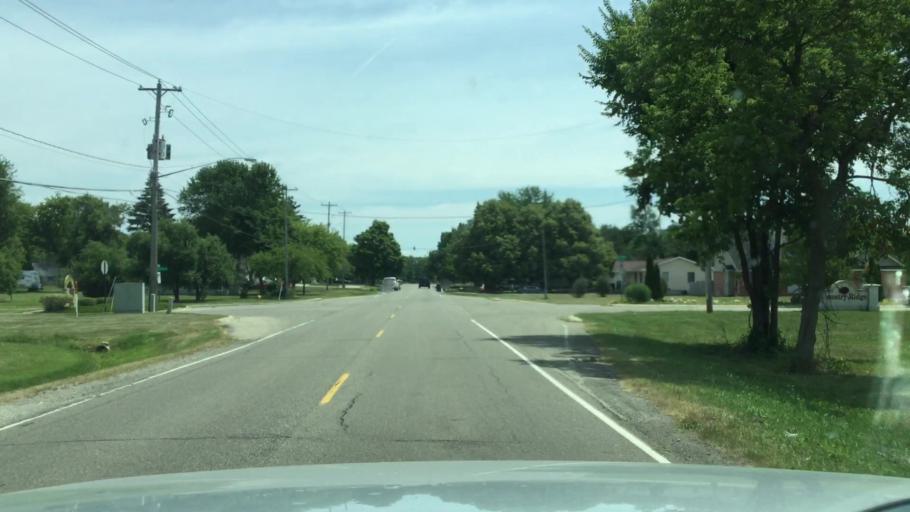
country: US
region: Michigan
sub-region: Genesee County
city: Swartz Creek
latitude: 43.0163
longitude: -83.7982
